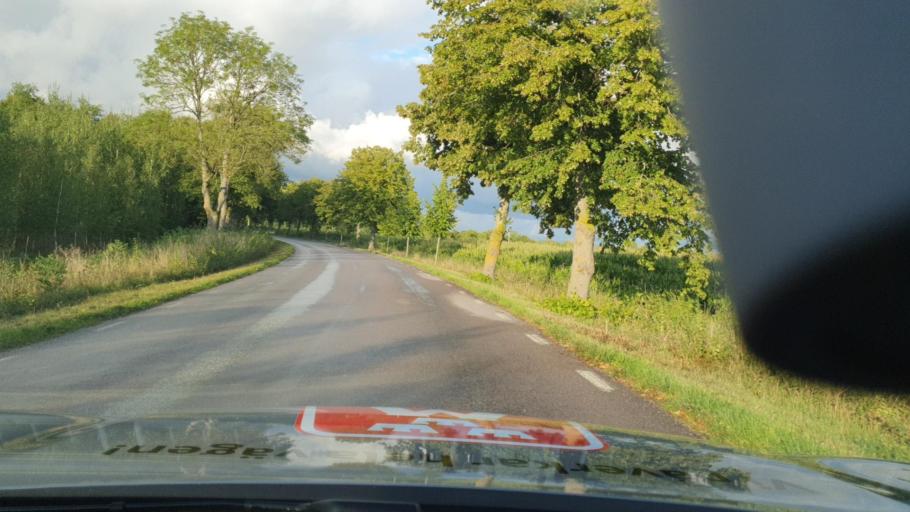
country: SE
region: Gotland
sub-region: Gotland
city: Klintehamn
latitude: 57.4110
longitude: 18.2187
